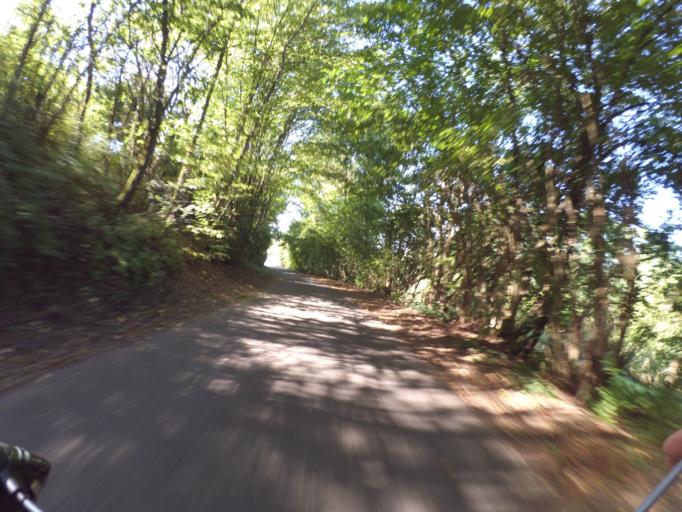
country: DE
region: Rheinland-Pfalz
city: Rivenich
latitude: 49.8703
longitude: 6.8456
